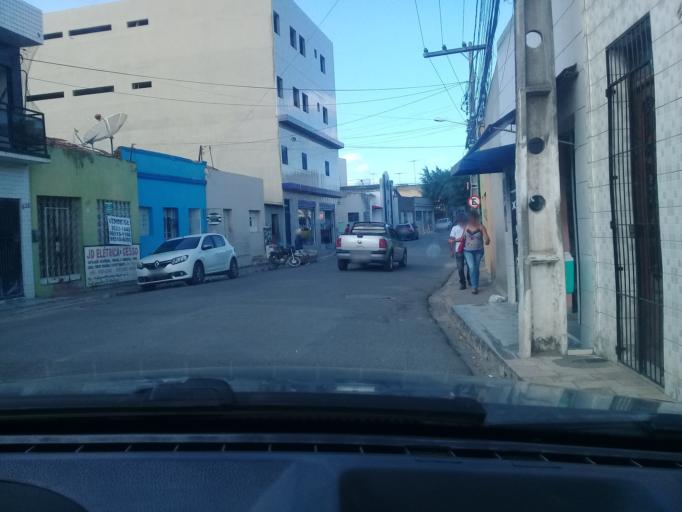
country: BR
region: Pernambuco
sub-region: Vitoria De Santo Antao
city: Vitoria de Santo Antao
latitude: -8.1197
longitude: -35.3027
